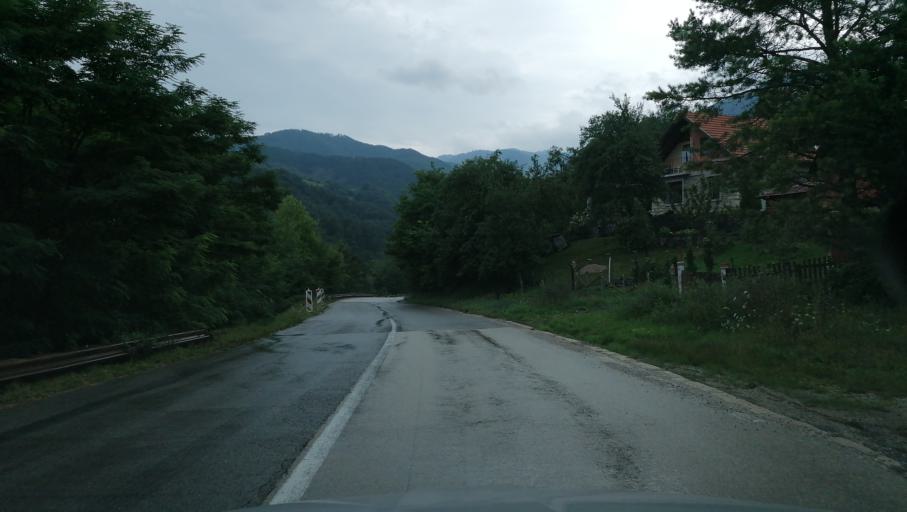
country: RS
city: Durici
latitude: 43.8003
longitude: 19.5084
